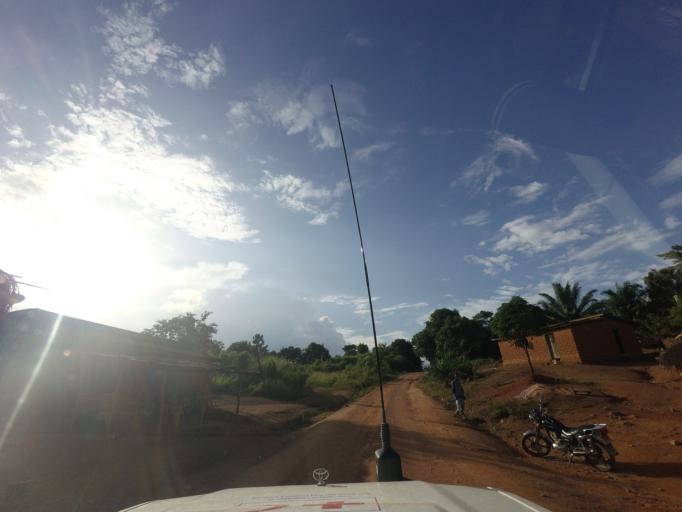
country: GN
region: Nzerekore
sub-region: Nzerekore Prefecture
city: Nzerekore
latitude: 7.6929
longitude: -8.8200
